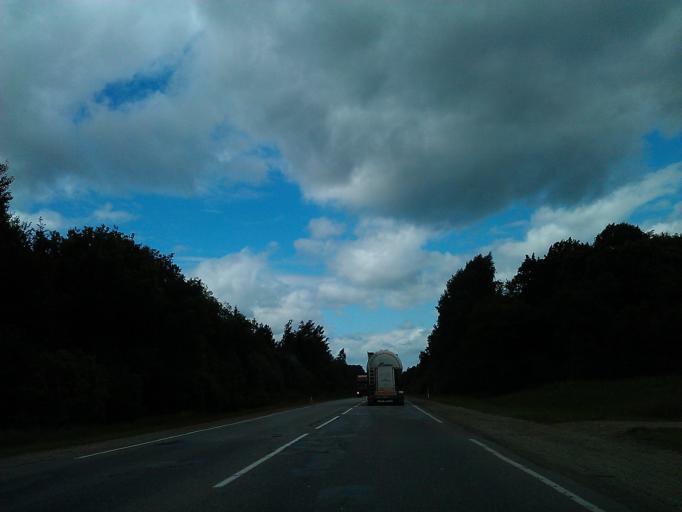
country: LV
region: Tukuma Rajons
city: Tukums
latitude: 56.9338
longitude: 23.1968
